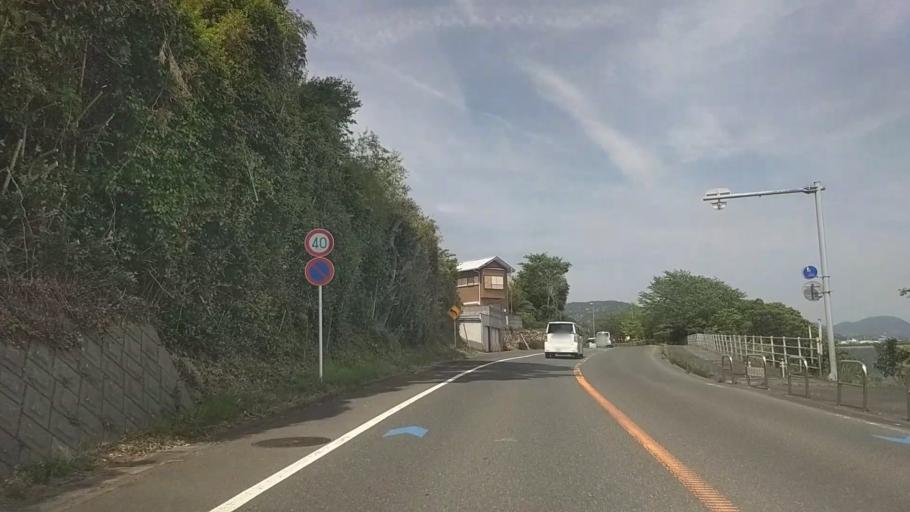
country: JP
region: Shizuoka
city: Kosai-shi
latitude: 34.7941
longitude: 137.6192
